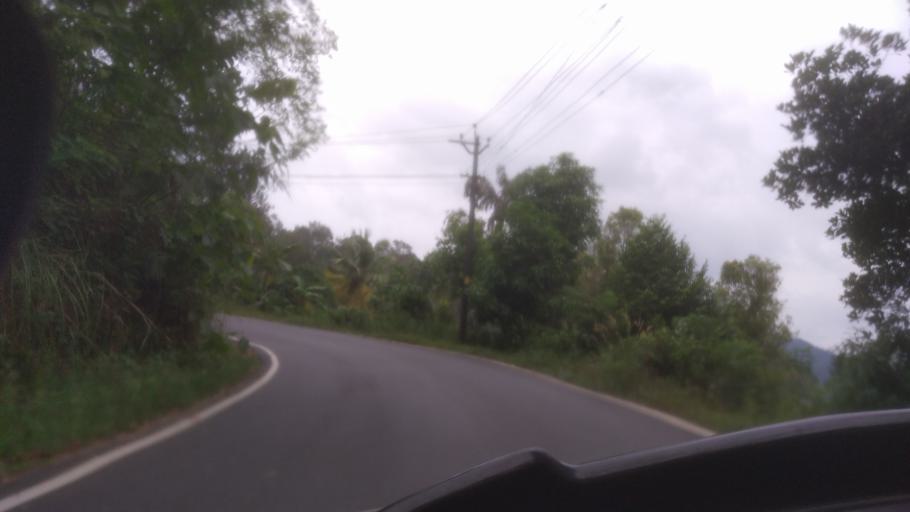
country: IN
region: Kerala
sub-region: Idukki
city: Idukki
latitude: 9.9650
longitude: 77.0031
